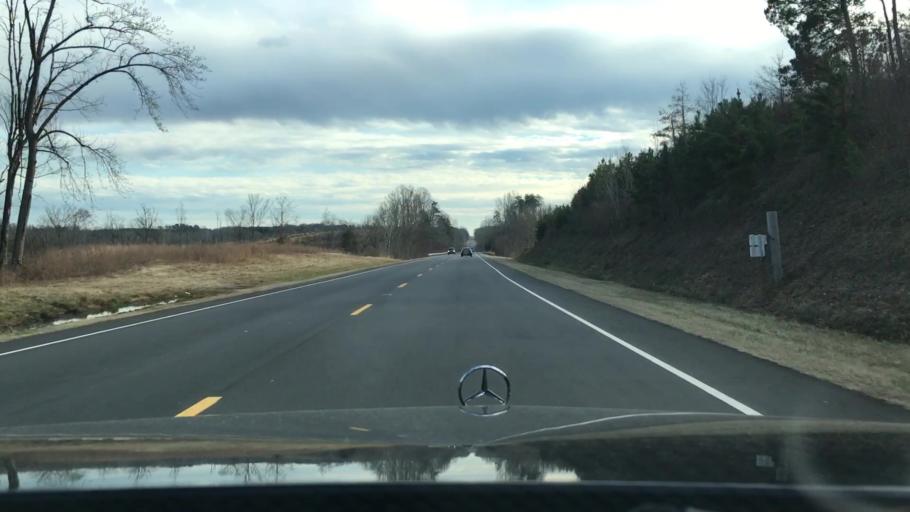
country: US
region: Virginia
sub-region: City of Danville
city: Danville
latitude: 36.5139
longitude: -79.3923
